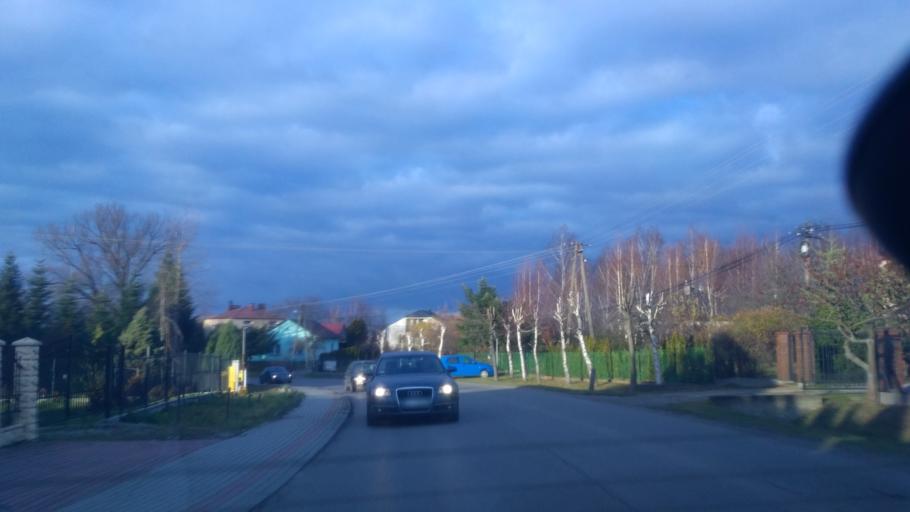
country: PL
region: Subcarpathian Voivodeship
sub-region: Powiat rzeszowski
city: Krasne
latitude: 50.0547
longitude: 22.1220
